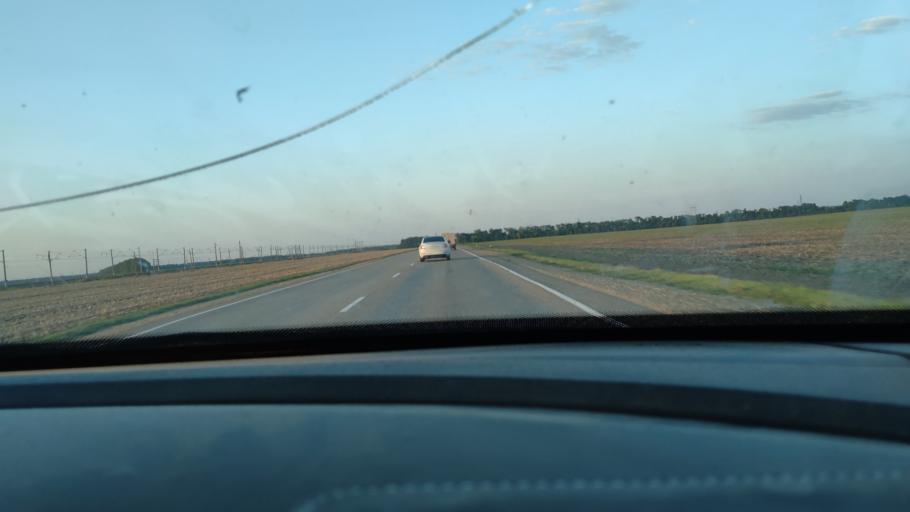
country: RU
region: Krasnodarskiy
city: Novominskaya
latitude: 46.3856
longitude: 38.9861
